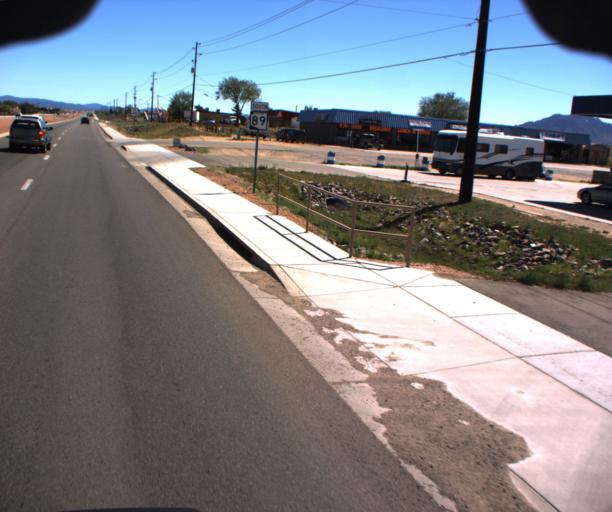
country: US
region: Arizona
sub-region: Yavapai County
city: Chino Valley
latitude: 34.7301
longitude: -112.4542
